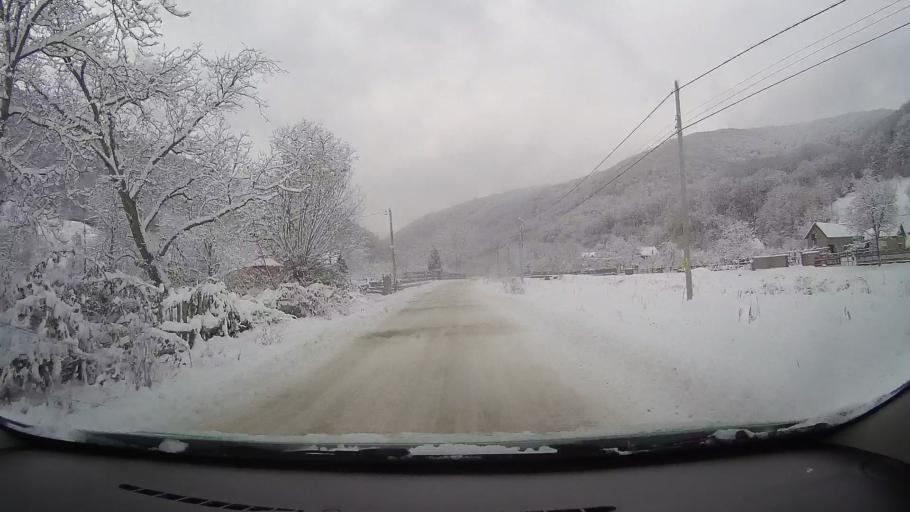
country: RO
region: Alba
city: Pianu de Sus
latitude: 45.8802
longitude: 23.4919
